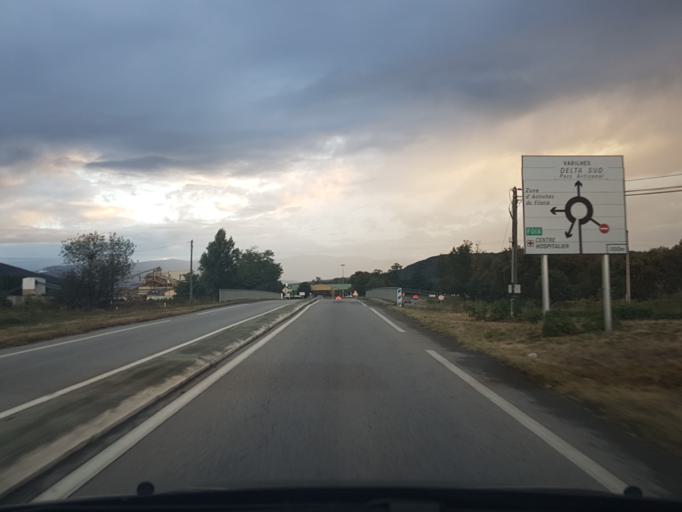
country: FR
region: Midi-Pyrenees
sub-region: Departement de l'Ariege
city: Verniolle
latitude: 43.0712
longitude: 1.6425
